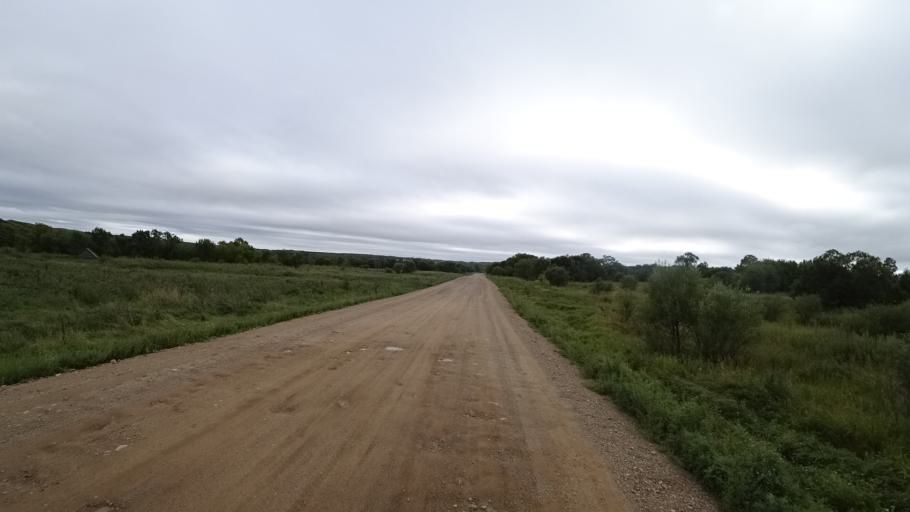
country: RU
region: Primorskiy
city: Rettikhovka
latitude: 44.1350
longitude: 132.6474
